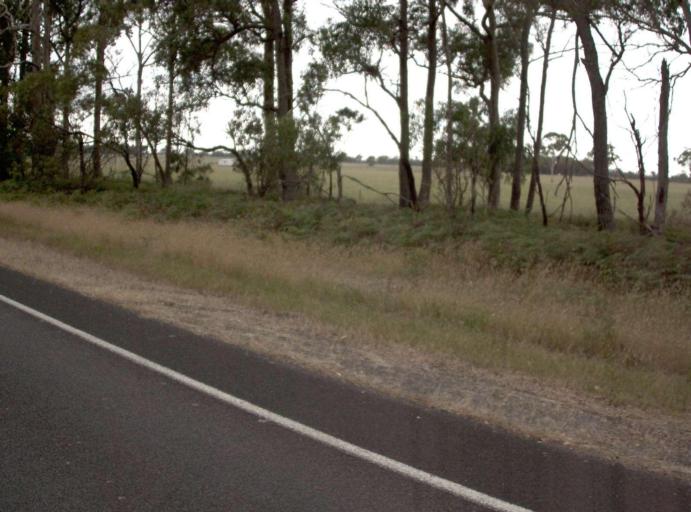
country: AU
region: Victoria
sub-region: Wellington
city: Sale
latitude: -38.4595
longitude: 146.9356
